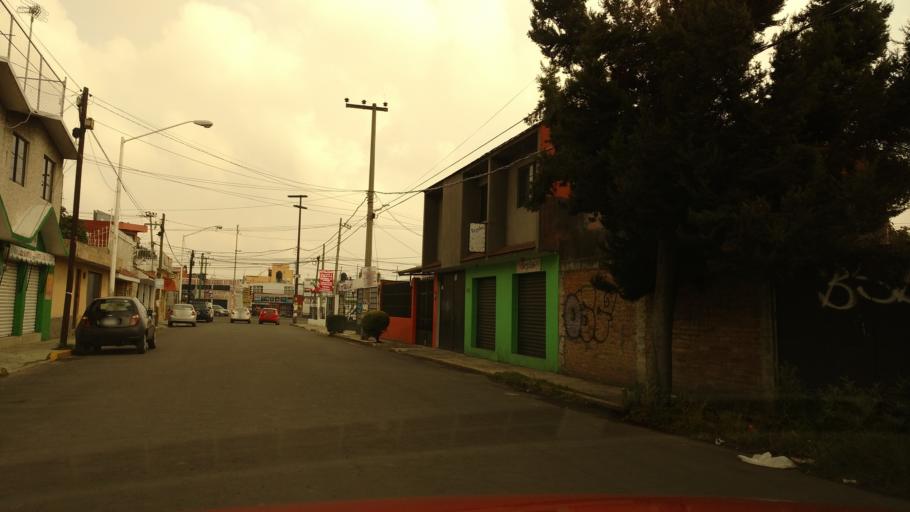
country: MX
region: Mexico
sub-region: Metepec
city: San Jorge Pueblo Nuevo
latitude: 19.2640
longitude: -99.6347
